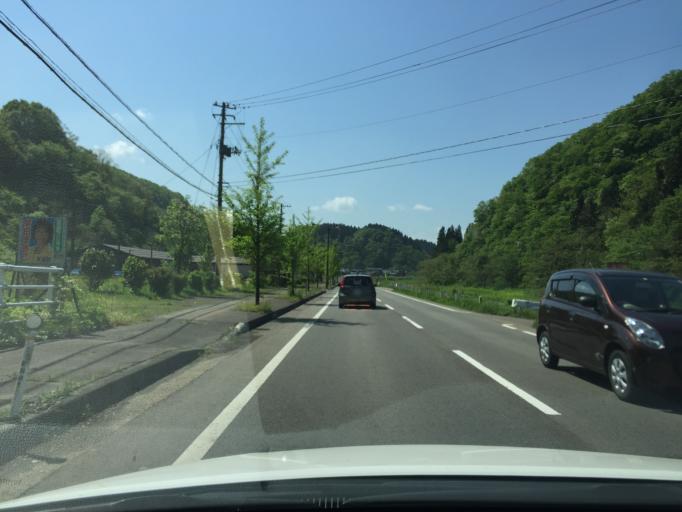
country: JP
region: Niigata
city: Kamo
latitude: 37.6243
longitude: 139.1040
